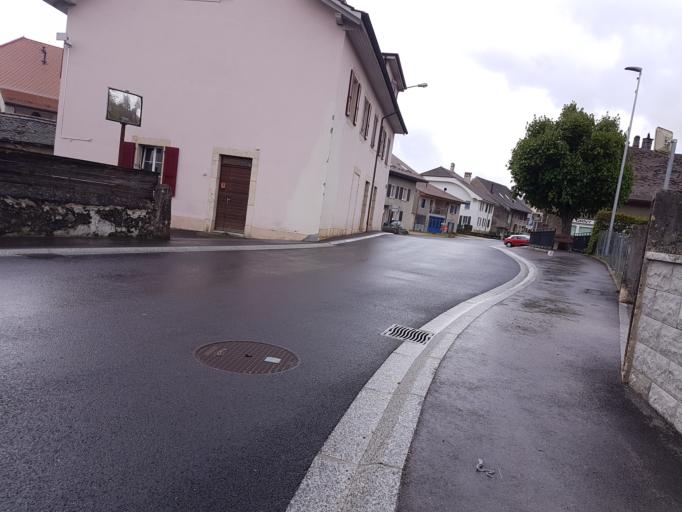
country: CH
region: Vaud
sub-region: Morges District
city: Orny
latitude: 46.6678
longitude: 6.5261
